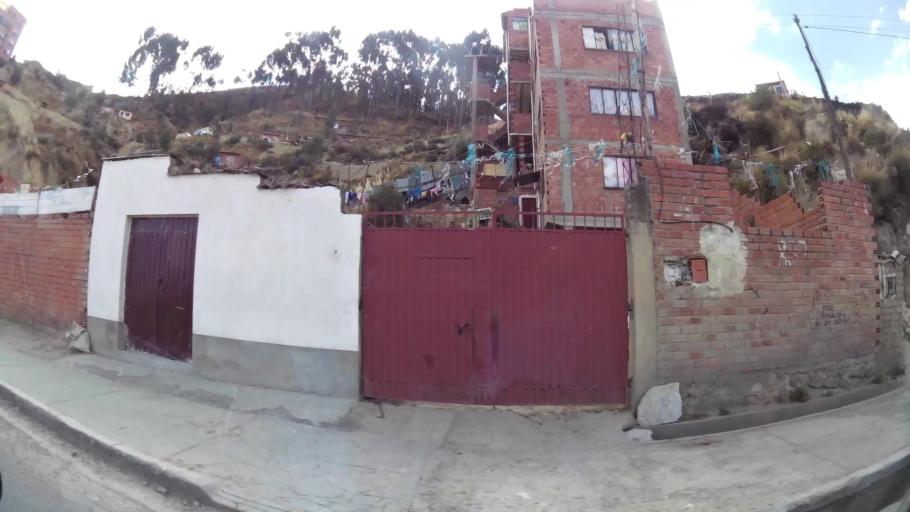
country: BO
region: La Paz
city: La Paz
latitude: -16.4682
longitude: -68.1198
